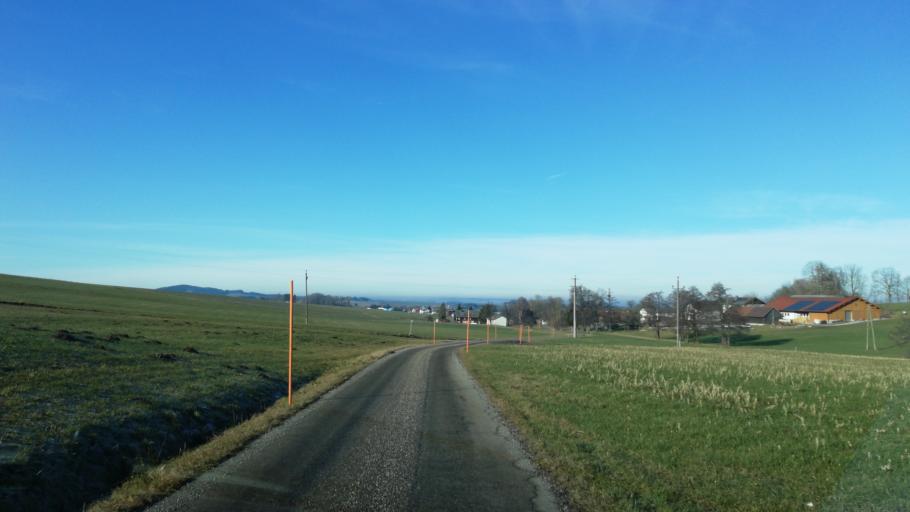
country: AT
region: Upper Austria
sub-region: Politischer Bezirk Vocklabruck
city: Zell am Pettenfirst
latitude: 48.1458
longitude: 13.5910
